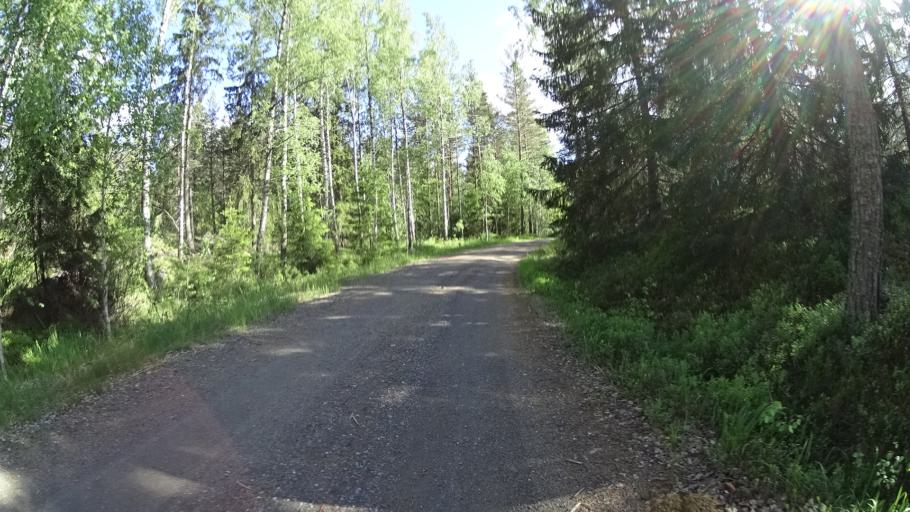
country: FI
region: Varsinais-Suomi
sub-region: Salo
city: Kisko
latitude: 60.1676
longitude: 23.4899
